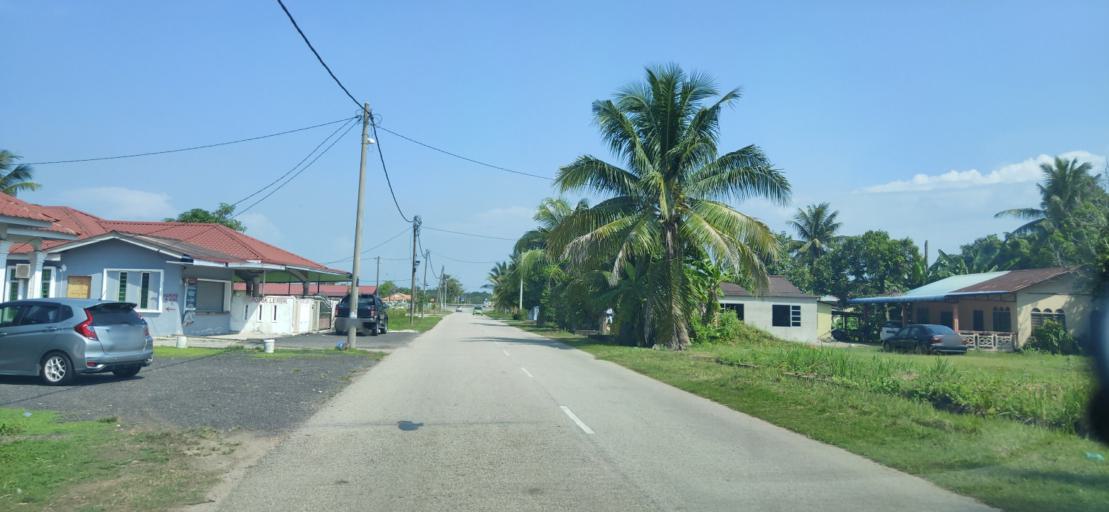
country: MY
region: Kedah
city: Sungai Petani
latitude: 5.6601
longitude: 100.4674
